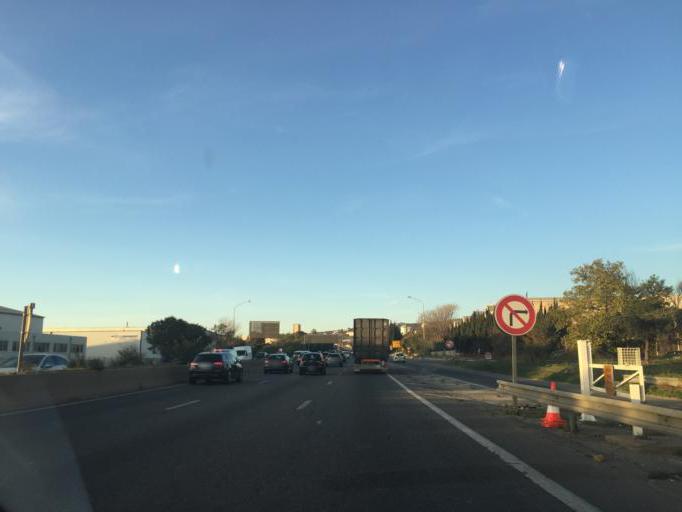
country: FR
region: Provence-Alpes-Cote d'Azur
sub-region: Departement des Bouches-du-Rhone
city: Marseille 14
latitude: 43.3333
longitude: 5.3776
